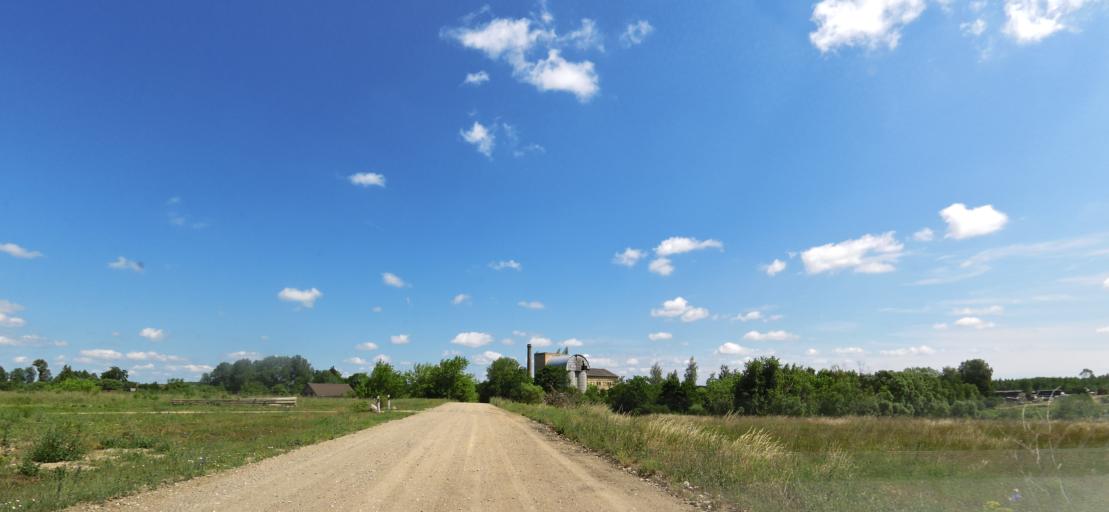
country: LT
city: Nemencine
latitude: 54.8706
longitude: 25.5359
